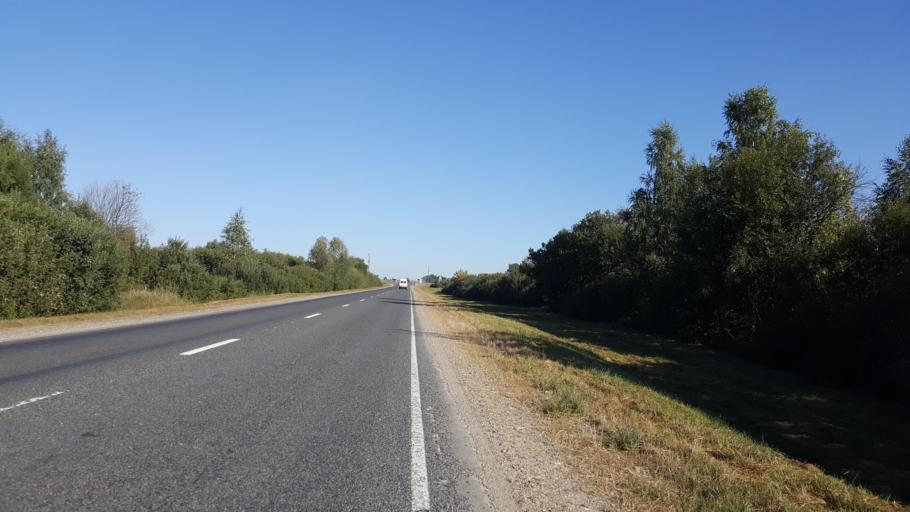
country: BY
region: Brest
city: Kamyanyets
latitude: 52.3927
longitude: 23.7862
